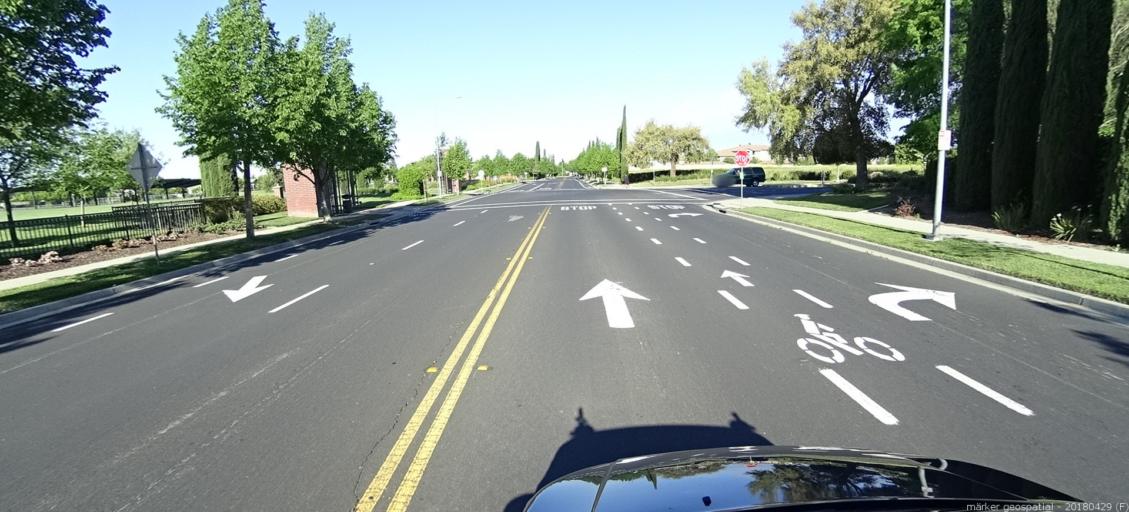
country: US
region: California
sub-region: Yolo County
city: West Sacramento
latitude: 38.5424
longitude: -121.5669
